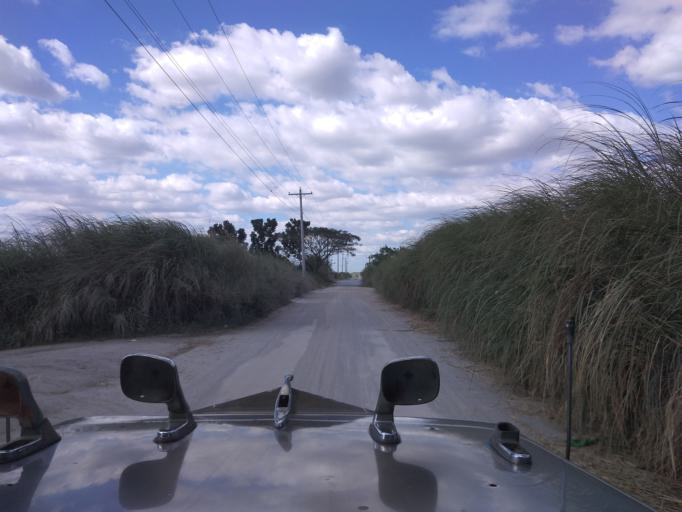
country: PH
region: Central Luzon
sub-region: Province of Pampanga
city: Magliman
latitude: 15.0462
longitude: 120.6278
